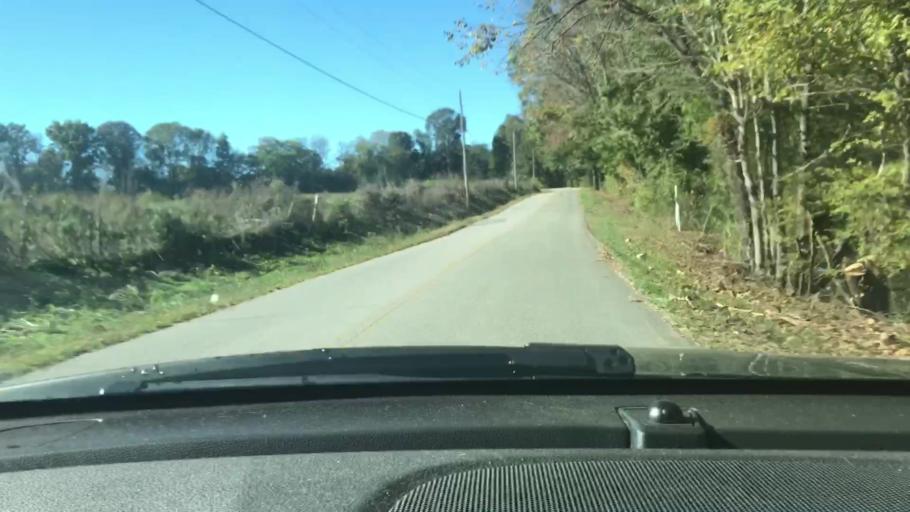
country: US
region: Tennessee
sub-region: Dickson County
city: Charlotte
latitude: 36.1800
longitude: -87.3071
